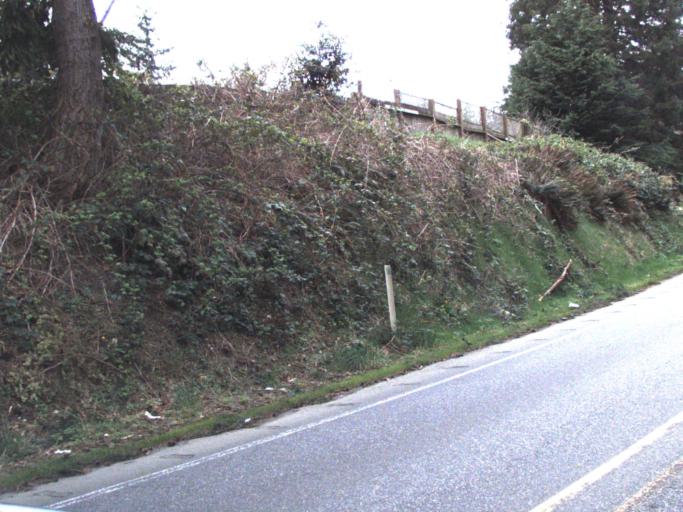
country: US
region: Washington
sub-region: King County
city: Federal Way
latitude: 47.3317
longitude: -122.3266
